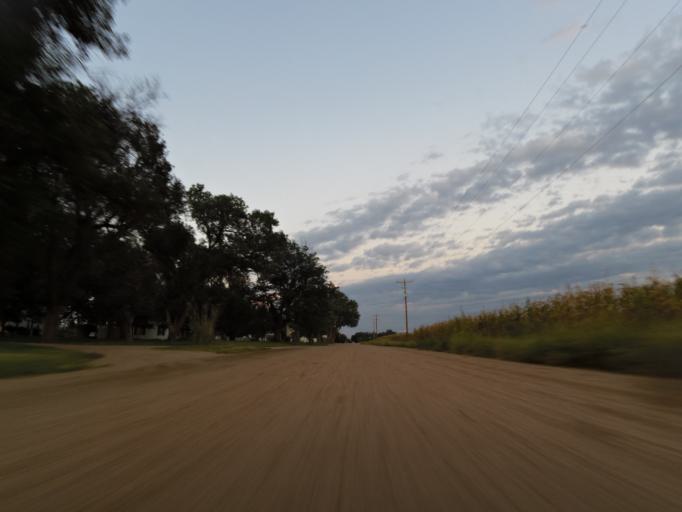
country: US
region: Kansas
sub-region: Reno County
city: South Hutchinson
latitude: 37.9555
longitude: -98.0337
